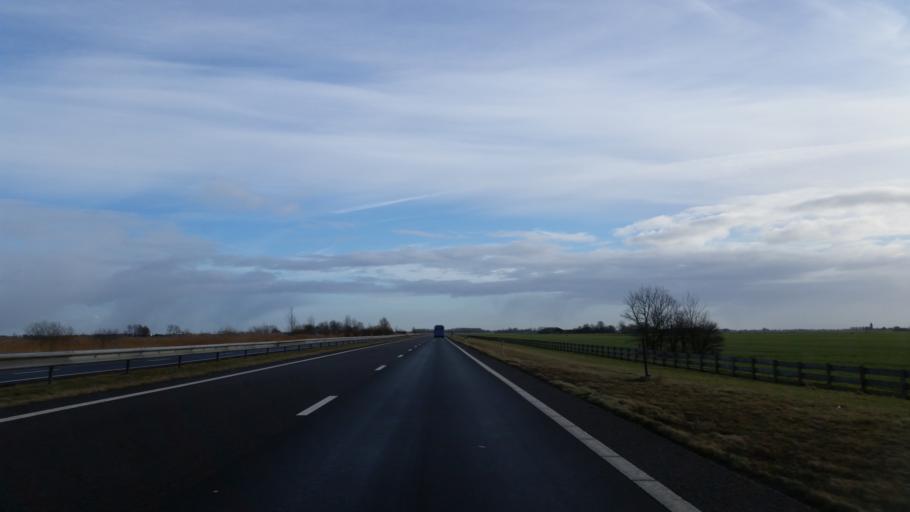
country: NL
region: Friesland
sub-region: Gemeente Boarnsterhim
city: Warten
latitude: 53.1703
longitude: 5.8730
